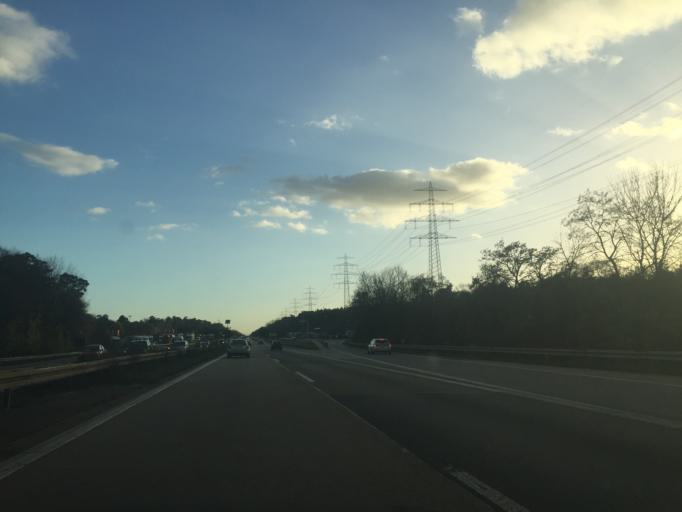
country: DE
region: Baden-Wuerttemberg
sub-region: Karlsruhe Region
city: Sandhausen
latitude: 49.3533
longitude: 8.6313
